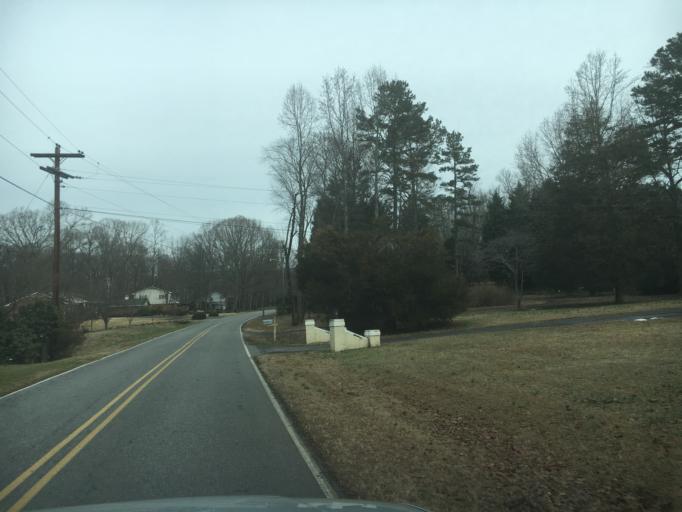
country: US
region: North Carolina
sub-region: Iredell County
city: Statesville
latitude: 35.7994
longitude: -80.8175
